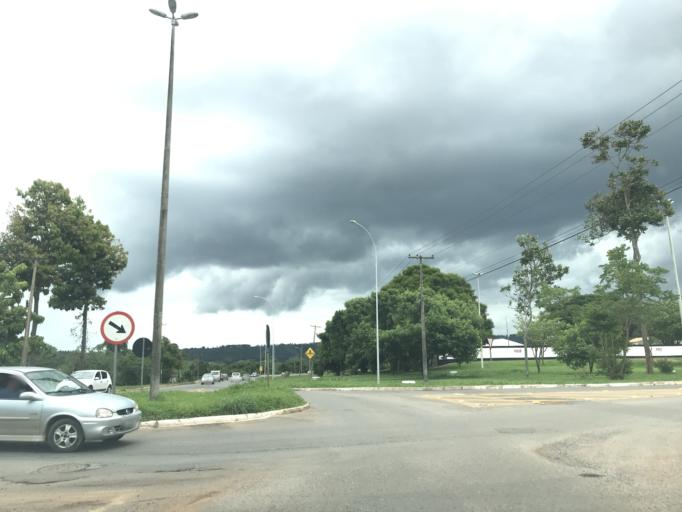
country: BR
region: Federal District
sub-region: Brasilia
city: Brasilia
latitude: -15.6505
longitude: -47.8133
